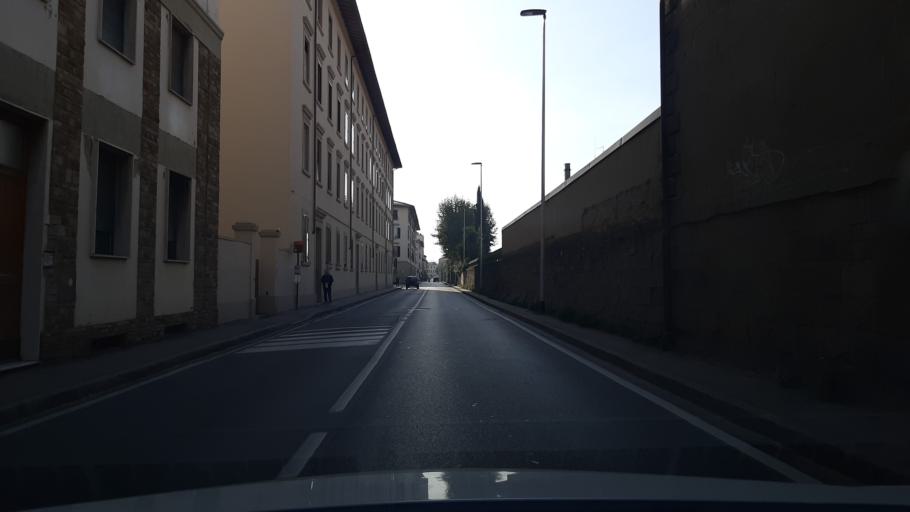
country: IT
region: Tuscany
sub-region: Province of Florence
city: Fiesole
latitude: 43.7763
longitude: 11.2797
